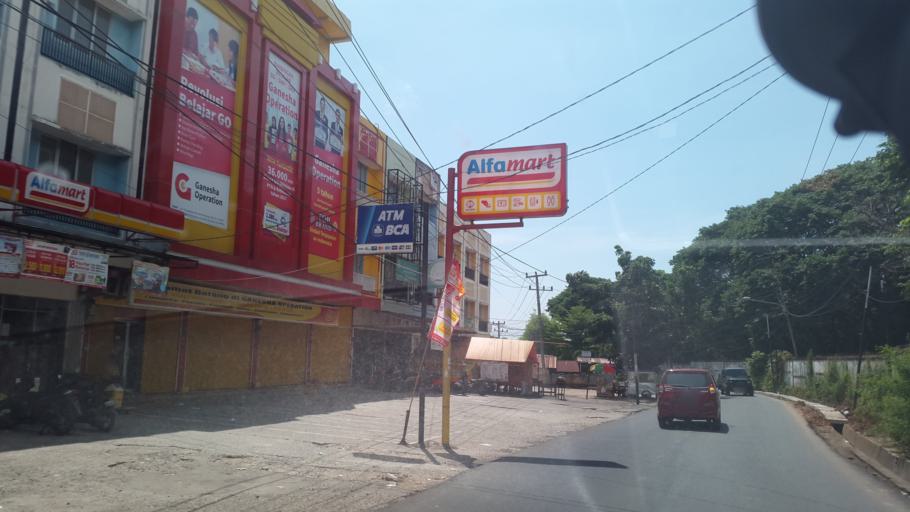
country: ID
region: South Sumatra
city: Plaju
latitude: -2.9959
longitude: 104.7266
